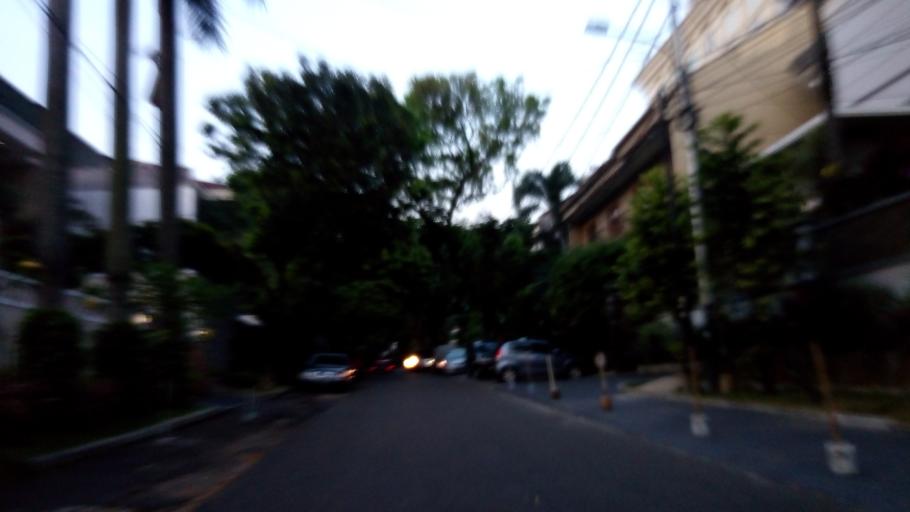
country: ID
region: Jakarta Raya
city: Jakarta
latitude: -6.2444
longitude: 106.7949
